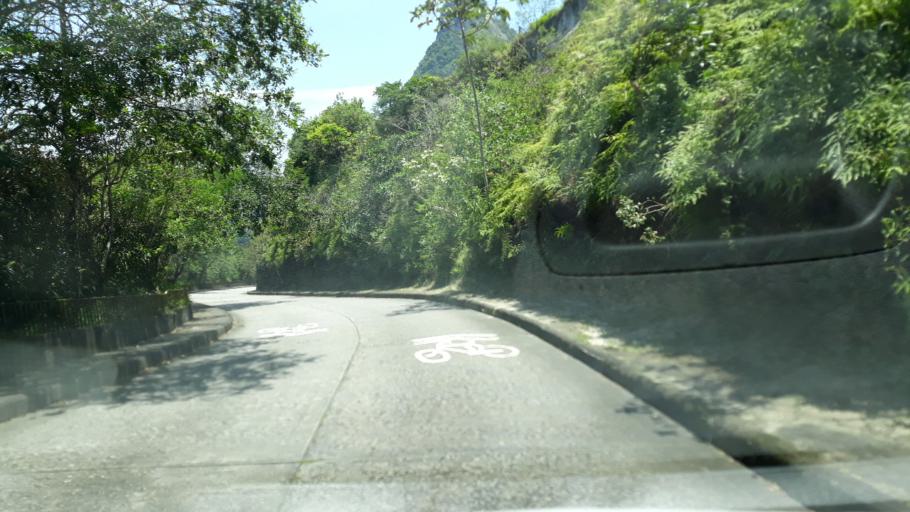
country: BR
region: Rio de Janeiro
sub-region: Rio De Janeiro
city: Rio de Janeiro
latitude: -22.9465
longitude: -43.1976
